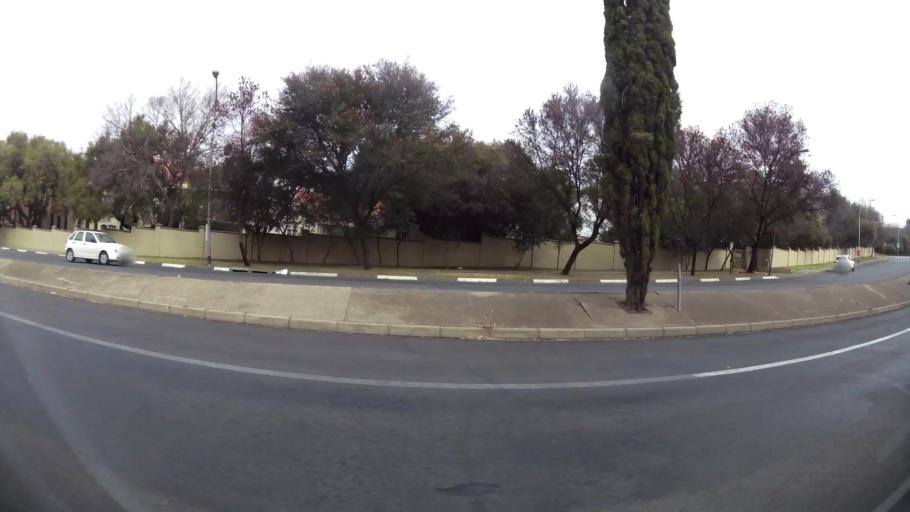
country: ZA
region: Orange Free State
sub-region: Mangaung Metropolitan Municipality
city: Bloemfontein
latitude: -29.1006
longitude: 26.2205
